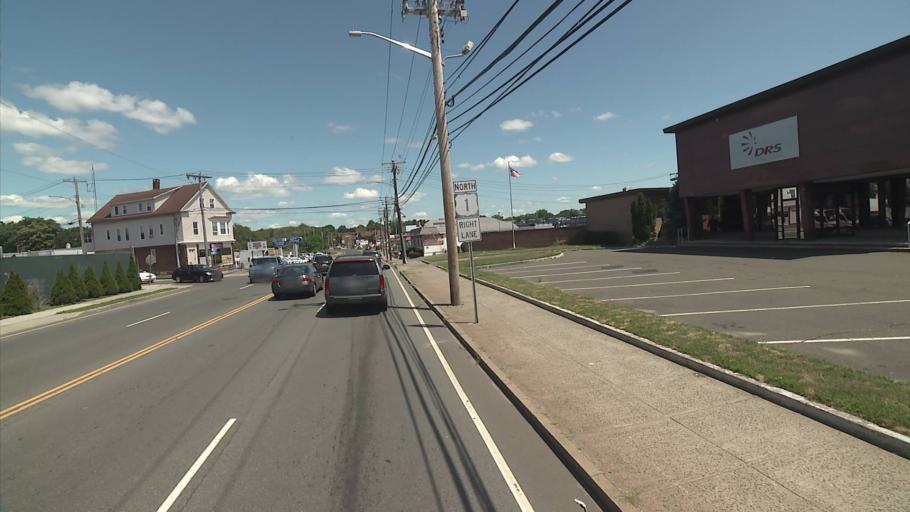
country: US
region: Connecticut
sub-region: Fairfield County
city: Bridgeport
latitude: 41.2014
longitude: -73.1911
